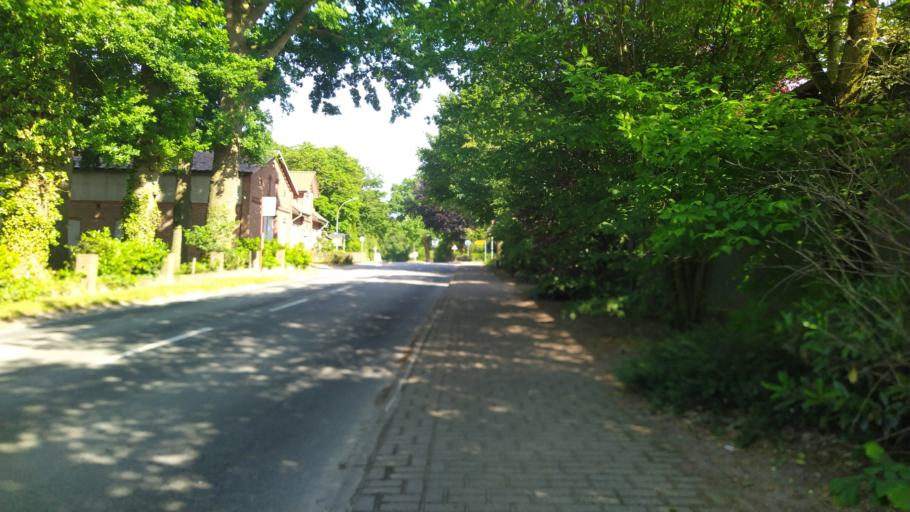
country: DE
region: Lower Saxony
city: Beckdorf
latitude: 53.4059
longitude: 9.6284
